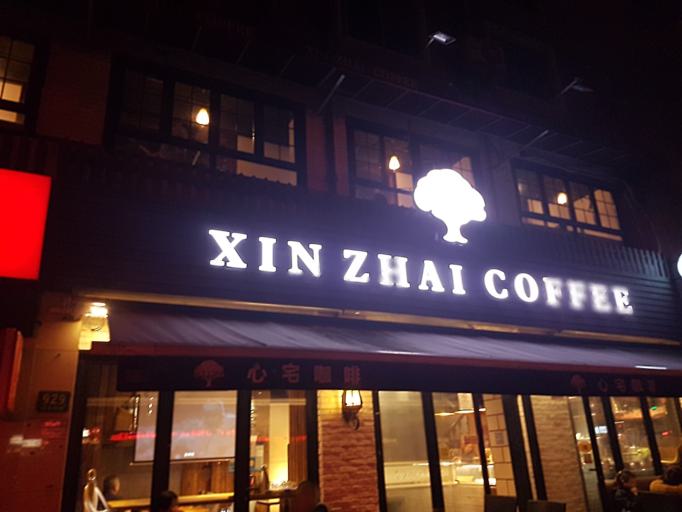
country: CN
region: Shanghai Shi
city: Changning
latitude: 31.1966
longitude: 121.3907
